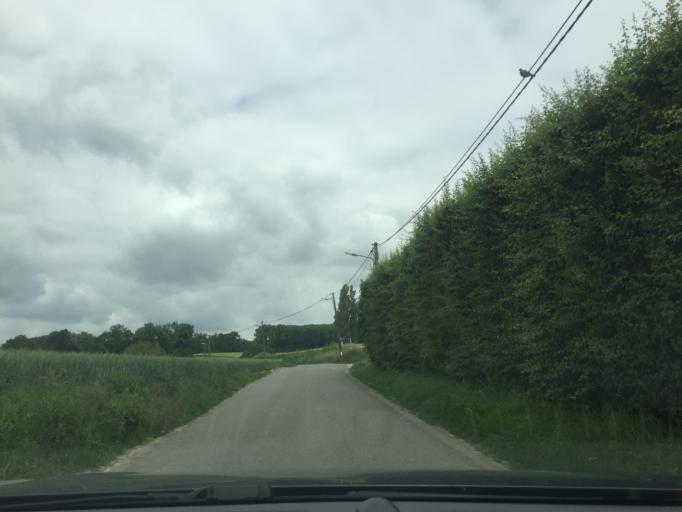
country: BE
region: Wallonia
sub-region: Province du Hainaut
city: Tournai
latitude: 50.6494
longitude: 3.3936
